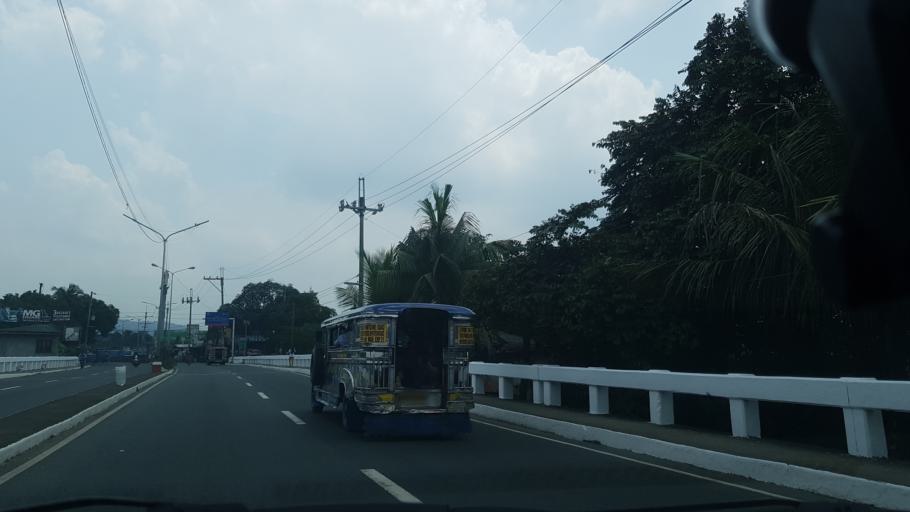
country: PH
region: Calabarzon
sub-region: Province of Rizal
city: San Mateo
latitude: 14.6792
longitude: 121.1100
